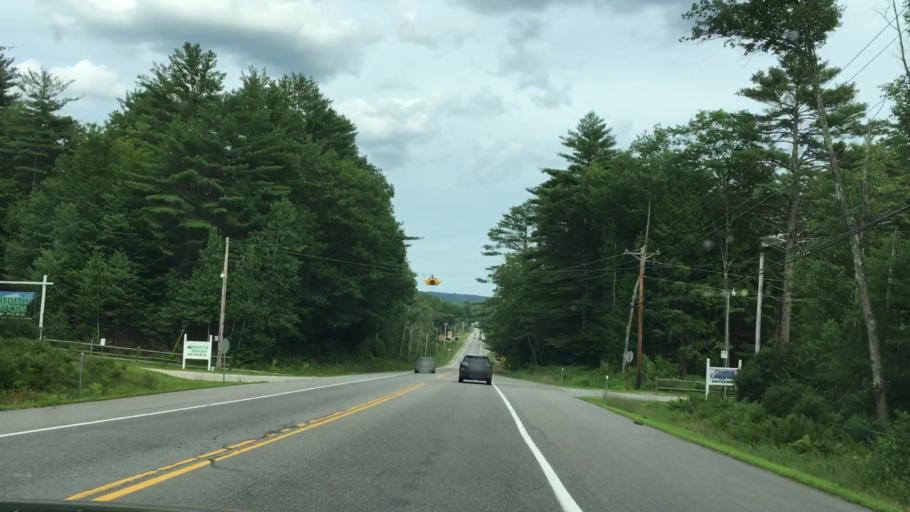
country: US
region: New Hampshire
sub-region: Grafton County
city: Ashland
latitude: 43.6196
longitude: -71.5864
